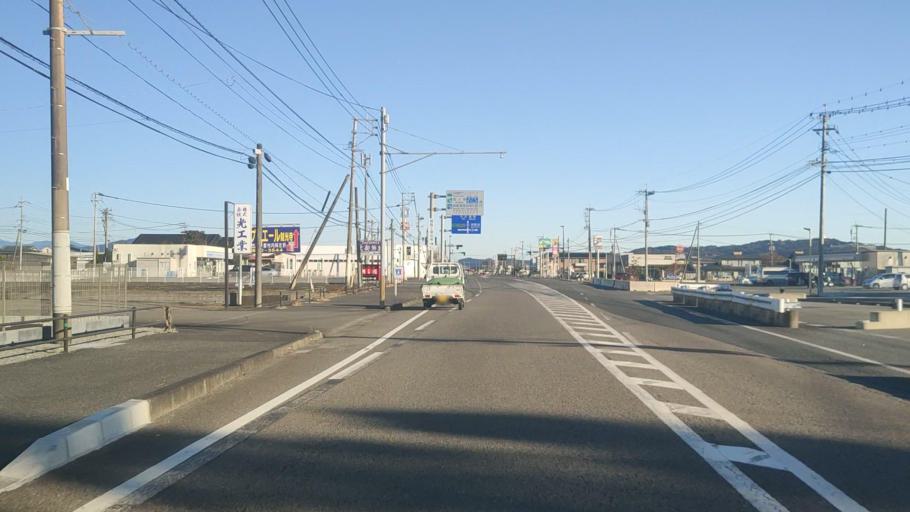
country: JP
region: Miyazaki
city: Nobeoka
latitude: 32.3954
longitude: 131.6290
